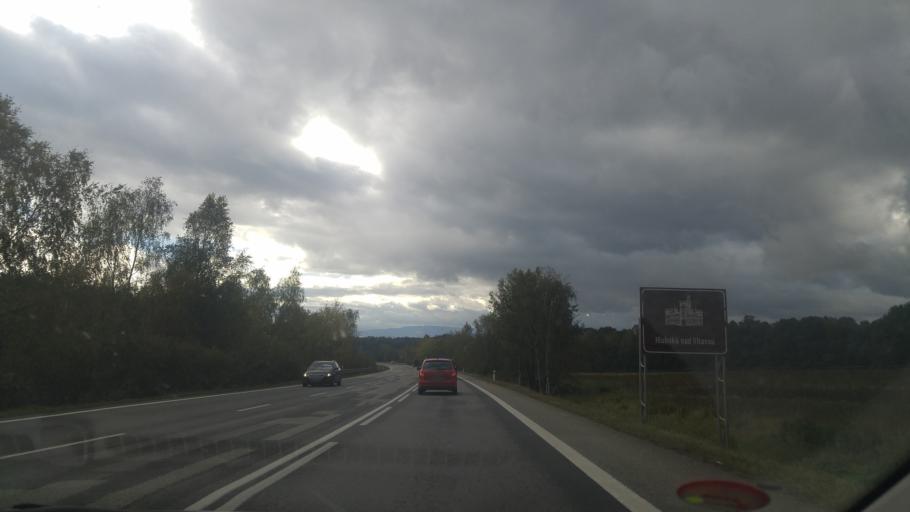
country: CZ
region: Jihocesky
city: Borek
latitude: 49.0627
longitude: 14.5253
